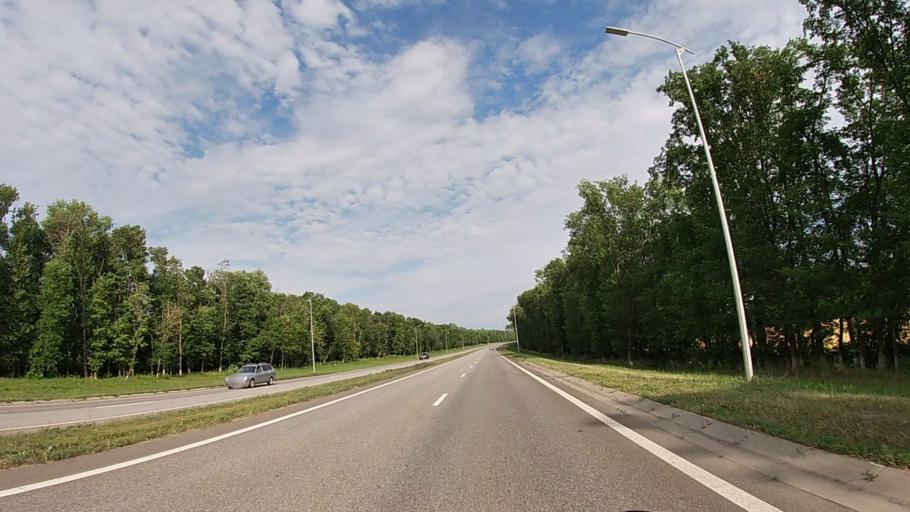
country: RU
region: Belgorod
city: Tomarovka
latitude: 50.6665
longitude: 36.3148
